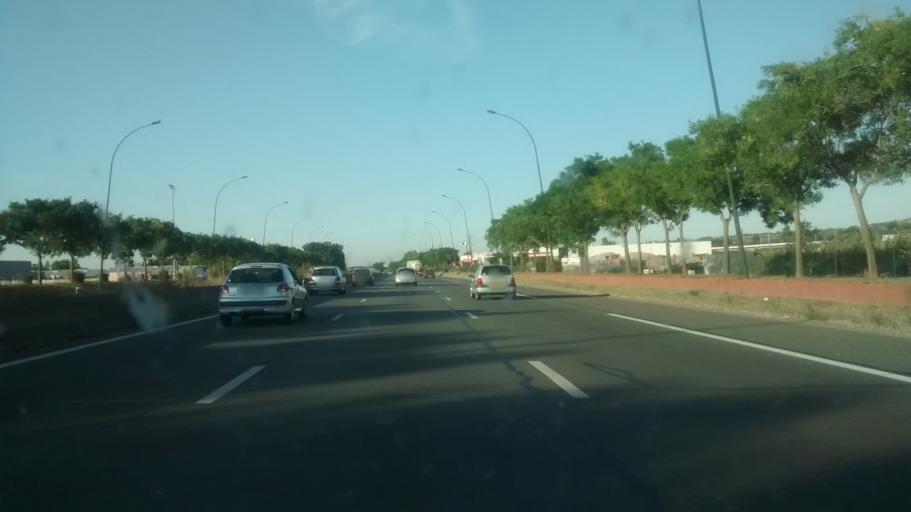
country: FR
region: Midi-Pyrenees
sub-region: Departement de la Haute-Garonne
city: Portet-sur-Garonne
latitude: 43.5457
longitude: 1.4020
